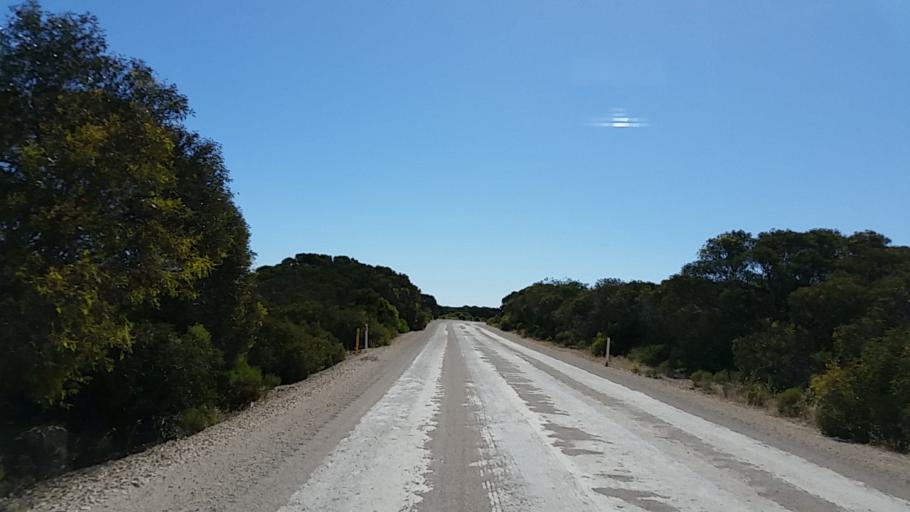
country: AU
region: South Australia
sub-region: Yorke Peninsula
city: Honiton
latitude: -35.2192
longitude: 137.0896
